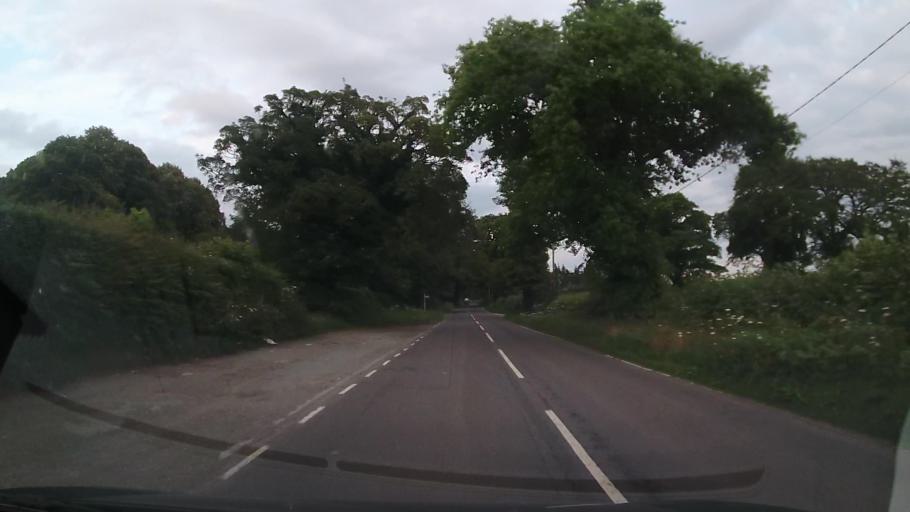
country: GB
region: England
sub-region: Shropshire
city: Great Ness
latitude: 52.7977
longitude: -2.9293
